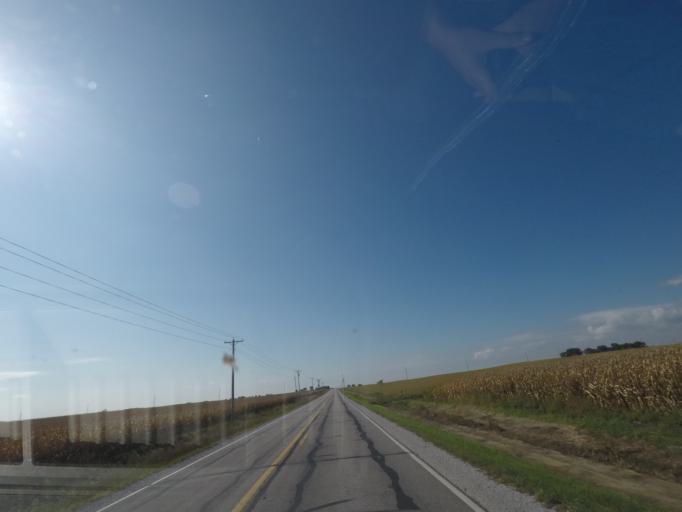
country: US
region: Iowa
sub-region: Story County
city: Nevada
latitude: 42.0389
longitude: -93.4059
